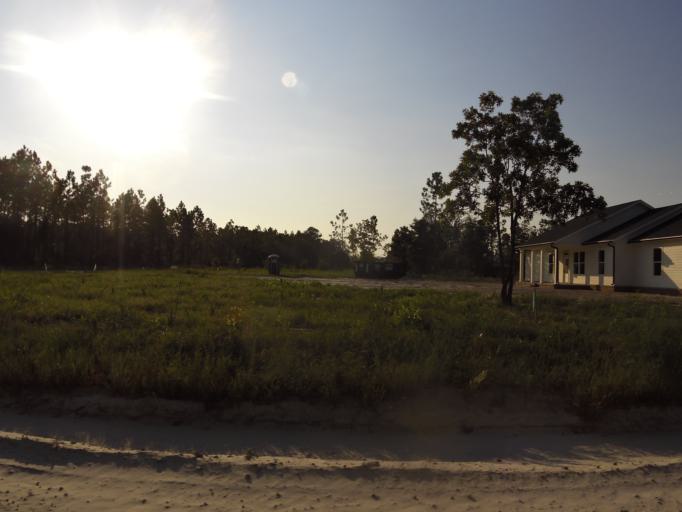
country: US
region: Florida
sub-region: Nassau County
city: Hilliard
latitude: 30.5539
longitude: -81.9933
